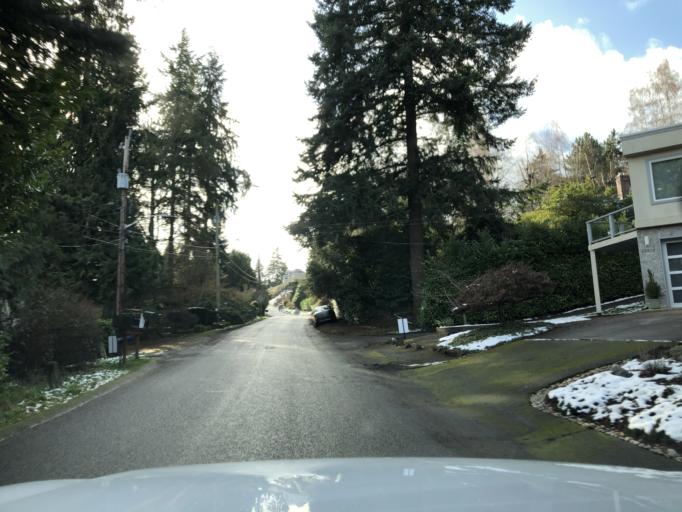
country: US
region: Washington
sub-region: King County
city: Lake Forest Park
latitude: 47.7204
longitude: -122.2831
